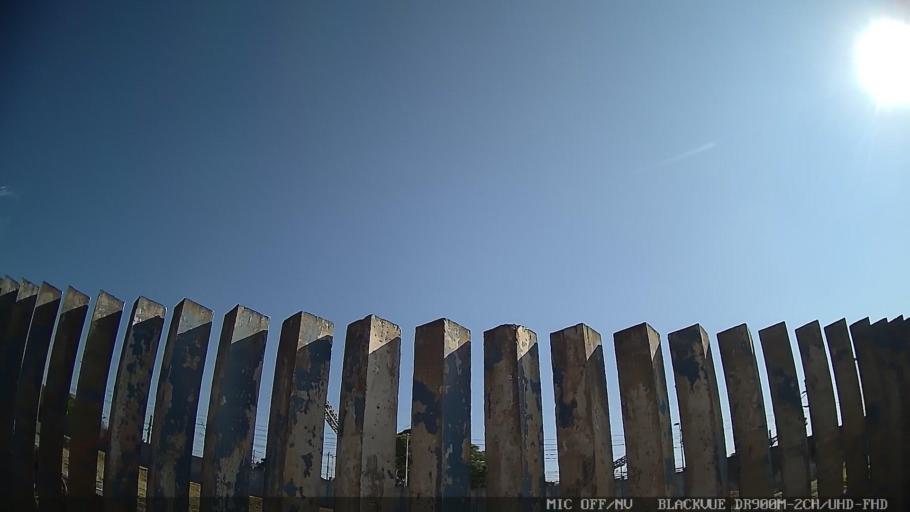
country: BR
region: Sao Paulo
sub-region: Ferraz De Vasconcelos
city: Ferraz de Vasconcelos
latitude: -23.5413
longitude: -46.4184
